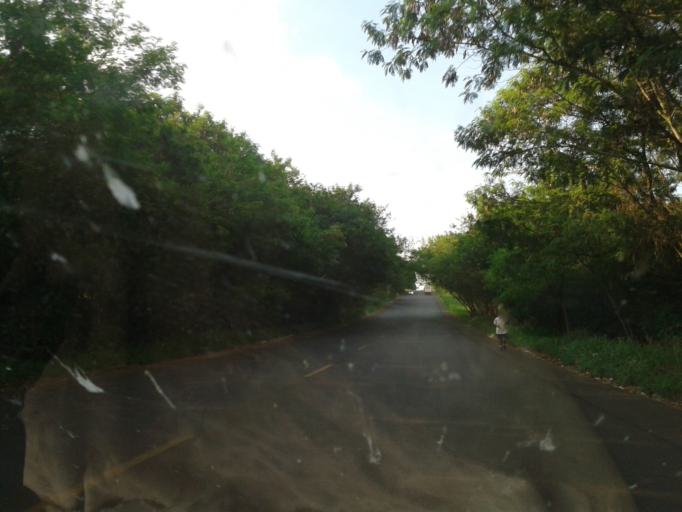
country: BR
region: Minas Gerais
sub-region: Uberlandia
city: Uberlandia
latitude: -18.9534
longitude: -48.3069
